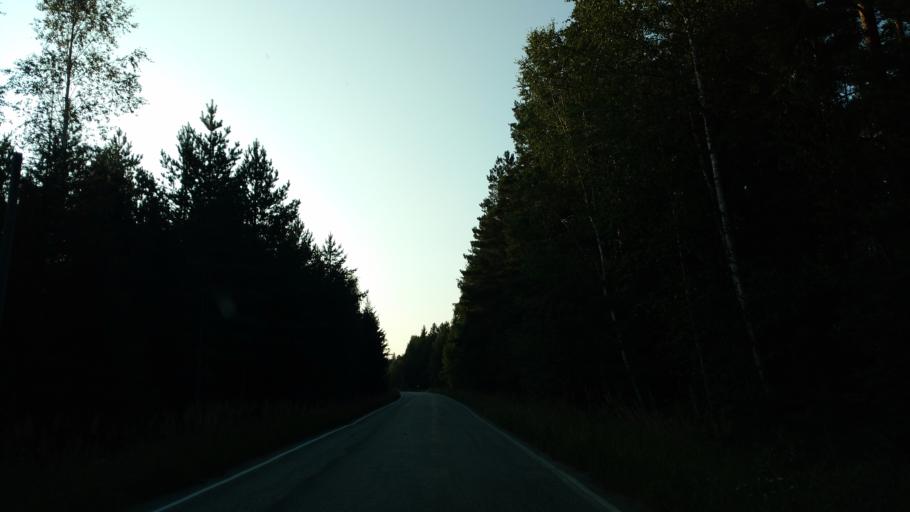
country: FI
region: Varsinais-Suomi
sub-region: Salo
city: Saerkisalo
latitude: 60.1853
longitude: 22.9607
